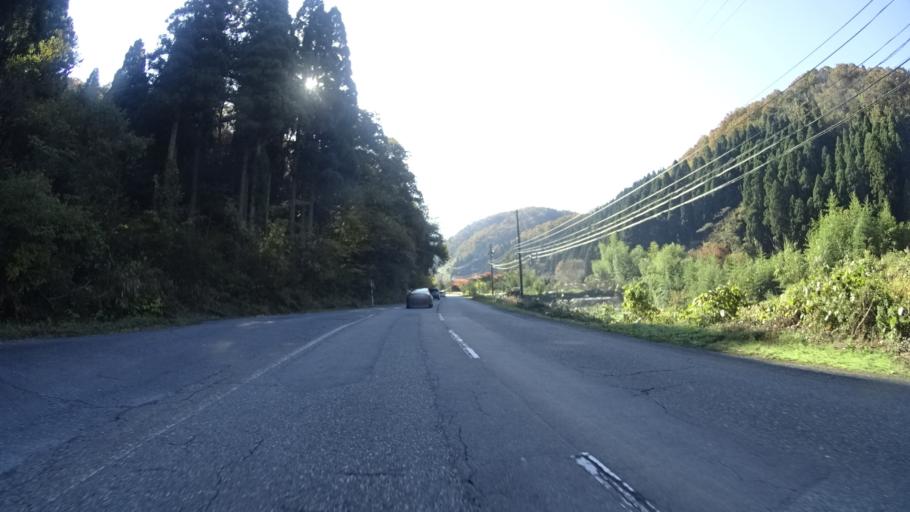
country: JP
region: Ishikawa
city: Komatsu
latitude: 36.3769
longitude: 136.5419
